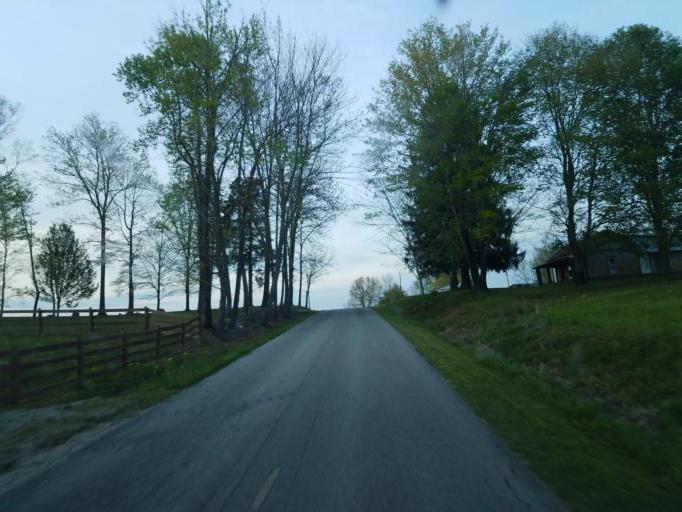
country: US
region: Kentucky
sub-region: Hart County
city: Munfordville
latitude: 37.2148
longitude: -85.6989
